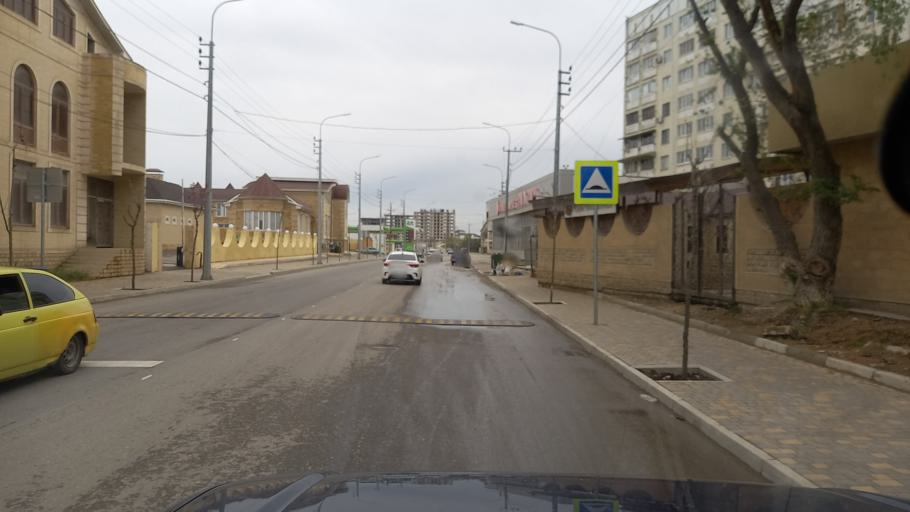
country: RU
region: Dagestan
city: Derbent
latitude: 42.0756
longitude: 48.2988
